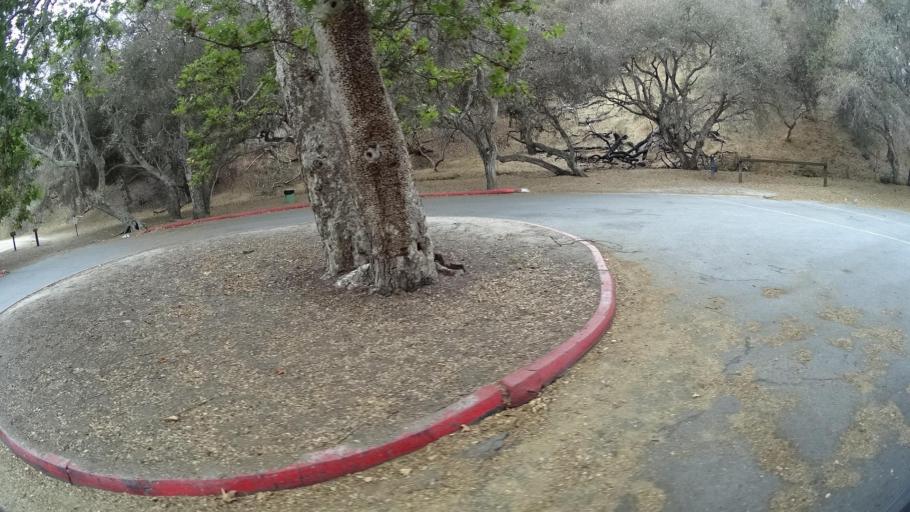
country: US
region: California
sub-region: Monterey County
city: Salinas
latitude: 36.6021
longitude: -121.6902
